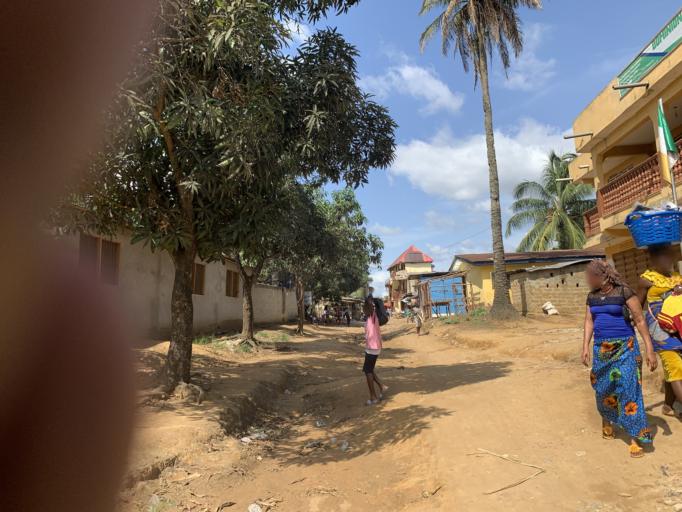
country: SL
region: Western Area
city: Waterloo
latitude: 8.3348
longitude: -13.0443
